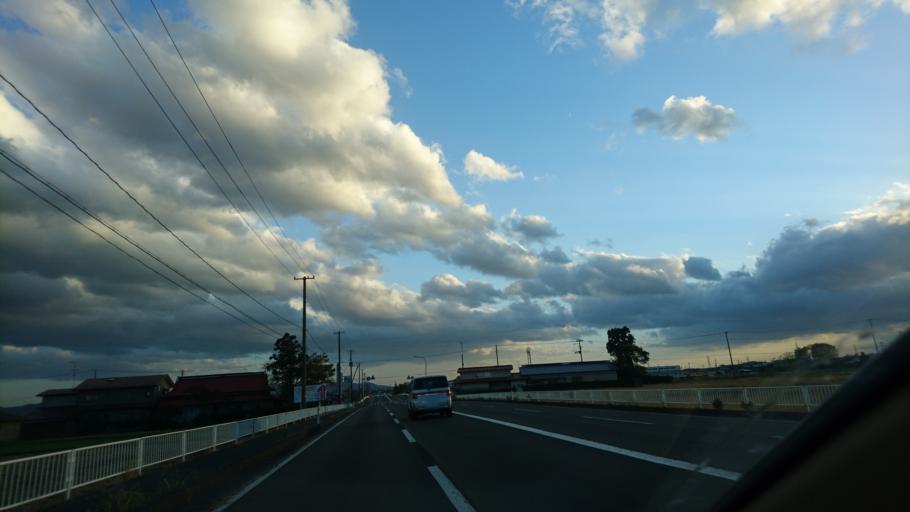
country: JP
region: Iwate
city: Mizusawa
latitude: 39.1613
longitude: 141.1330
